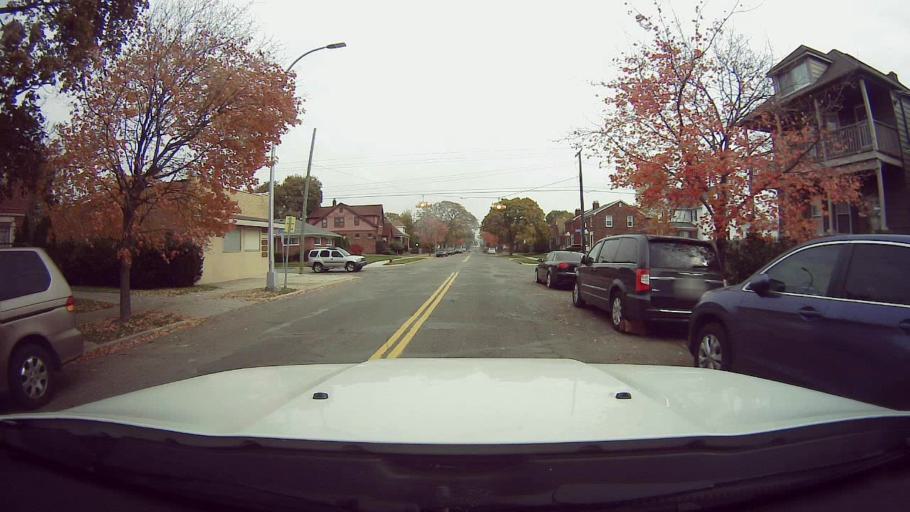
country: US
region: Michigan
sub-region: Wayne County
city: Hamtramck
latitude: 42.4035
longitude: -83.0497
